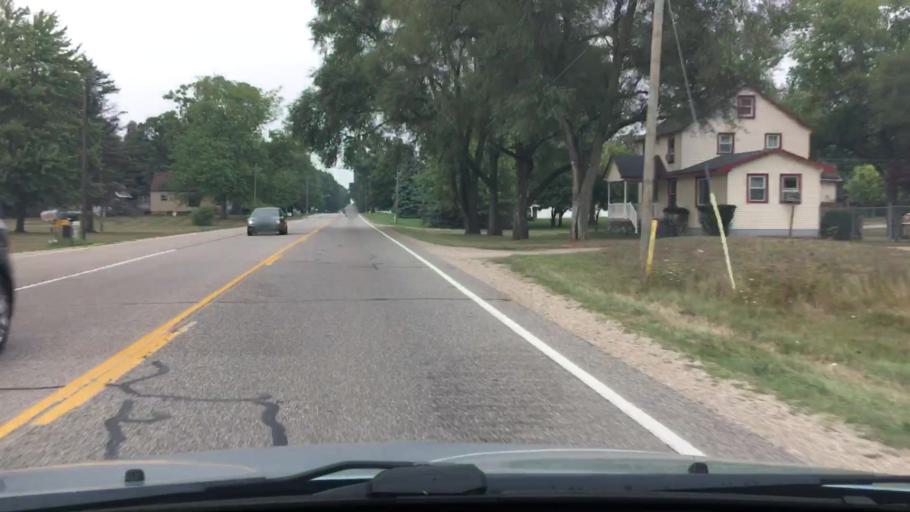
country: US
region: Michigan
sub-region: Ottawa County
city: Hudsonville
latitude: 42.8959
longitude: -85.9018
